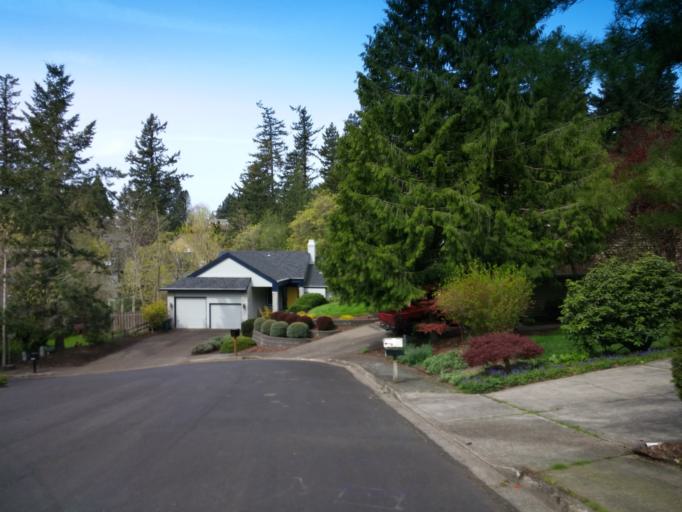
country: US
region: Oregon
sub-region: Washington County
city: Cedar Mill
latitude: 45.5320
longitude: -122.7967
